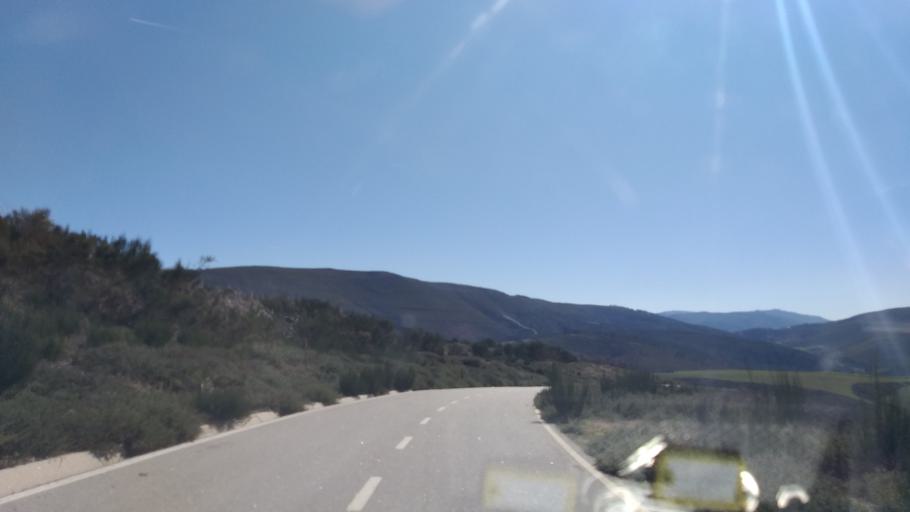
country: PT
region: Guarda
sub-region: Manteigas
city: Manteigas
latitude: 40.4652
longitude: -7.5026
